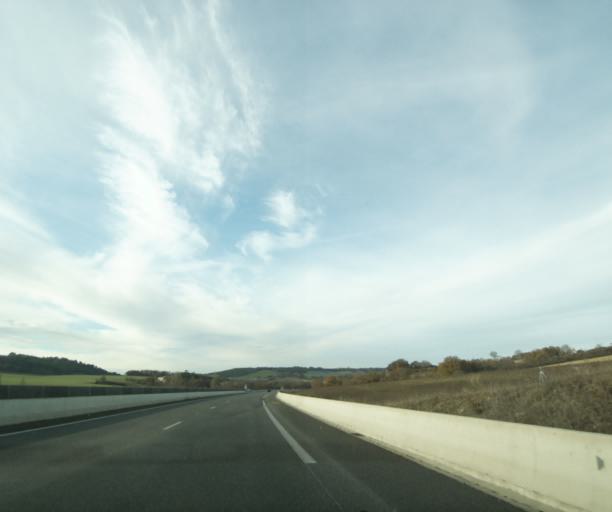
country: FR
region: Midi-Pyrenees
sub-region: Departement du Gers
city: Preignan
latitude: 43.6527
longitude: 0.6697
